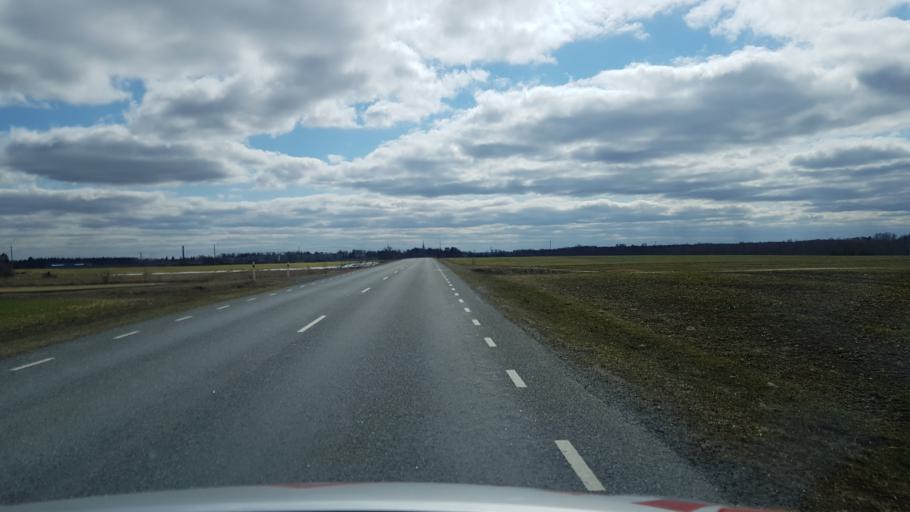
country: EE
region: Laeaene-Virumaa
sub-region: Kadrina vald
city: Kadrina
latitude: 59.3590
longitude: 26.1119
